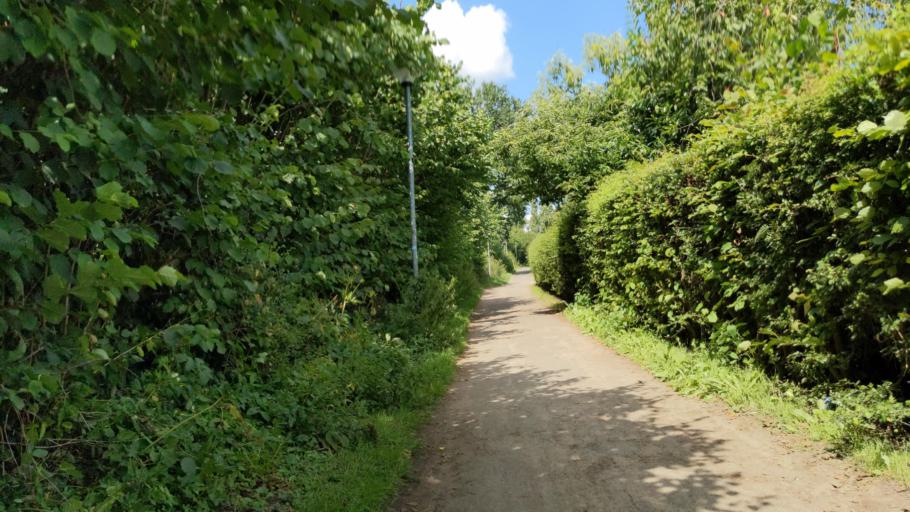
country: DE
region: Mecklenburg-Vorpommern
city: Selmsdorf
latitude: 53.9079
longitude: 10.8122
